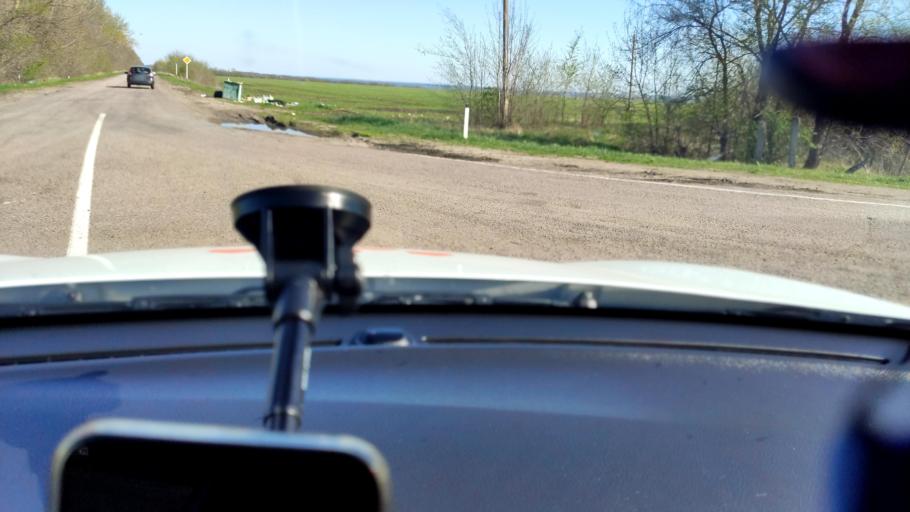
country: RU
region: Voronezj
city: Uryv-Pokrovka
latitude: 51.1464
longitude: 39.0619
